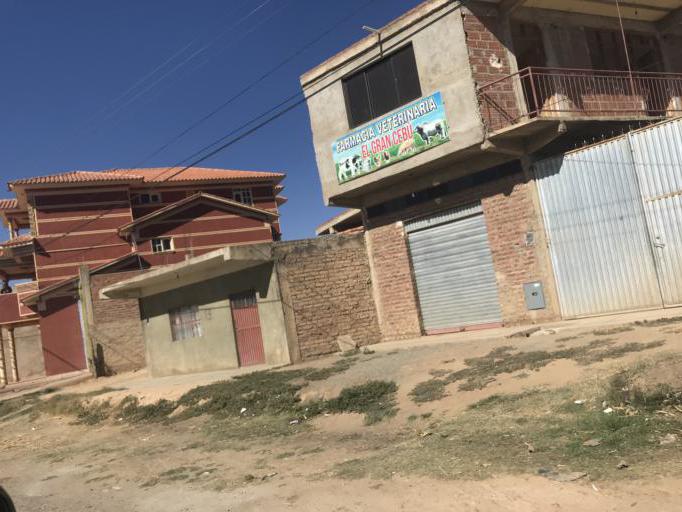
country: BO
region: Cochabamba
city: Cliza
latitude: -17.5871
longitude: -65.9212
